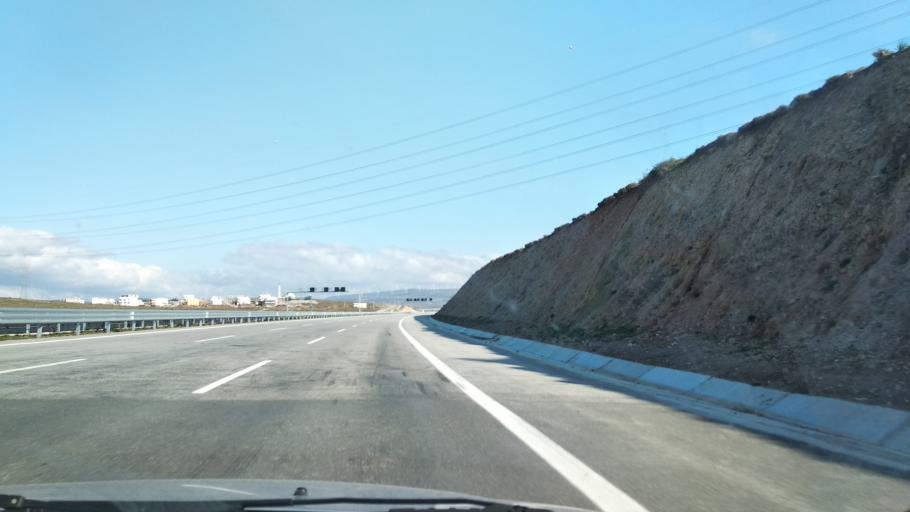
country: TR
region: Izmir
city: Yenisakran
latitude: 38.8527
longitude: 27.0557
